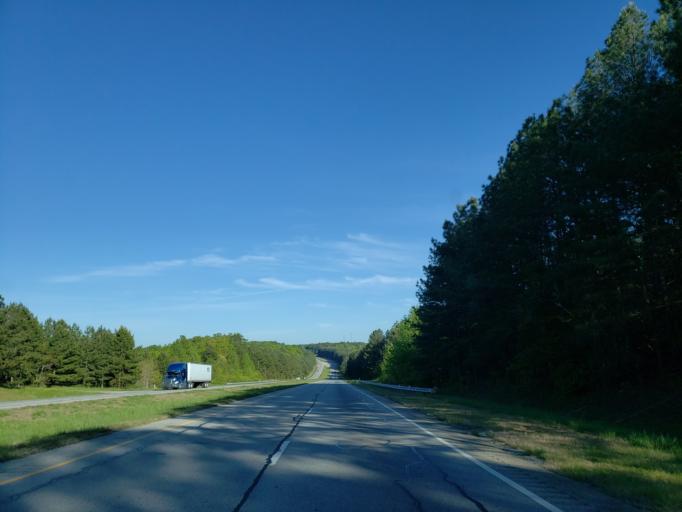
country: US
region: Georgia
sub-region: Polk County
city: Rockmart
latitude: 33.9346
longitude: -84.9669
